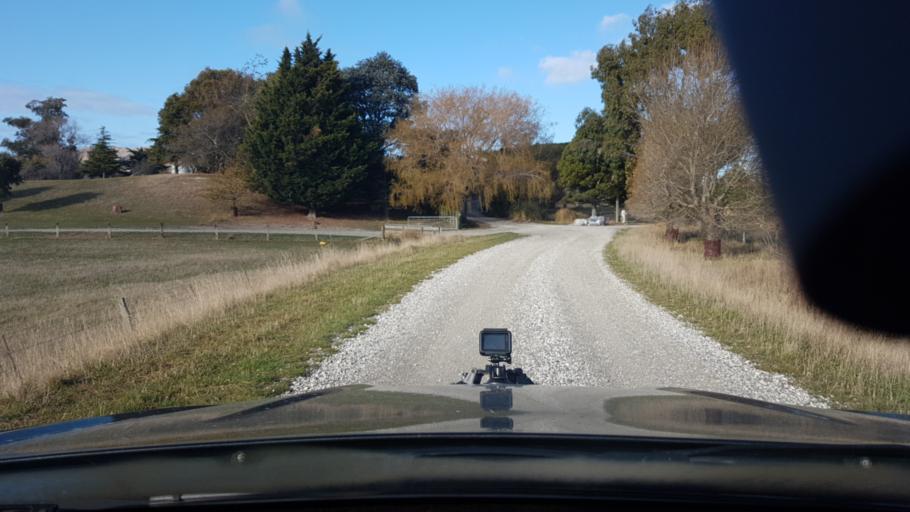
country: NZ
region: Marlborough
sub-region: Marlborough District
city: Blenheim
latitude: -41.8416
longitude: 174.1234
